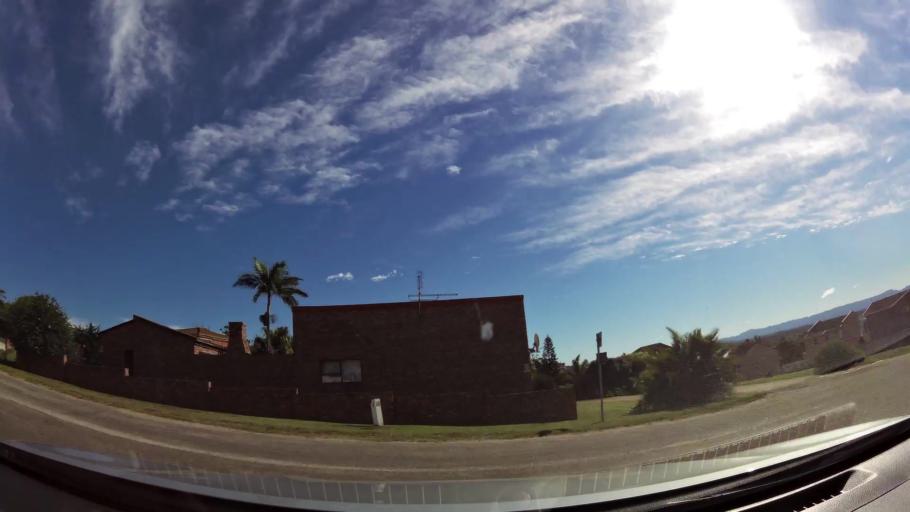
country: ZA
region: Eastern Cape
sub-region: Cacadu District Municipality
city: Jeffrey's Bay
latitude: -34.0192
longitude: 24.9230
